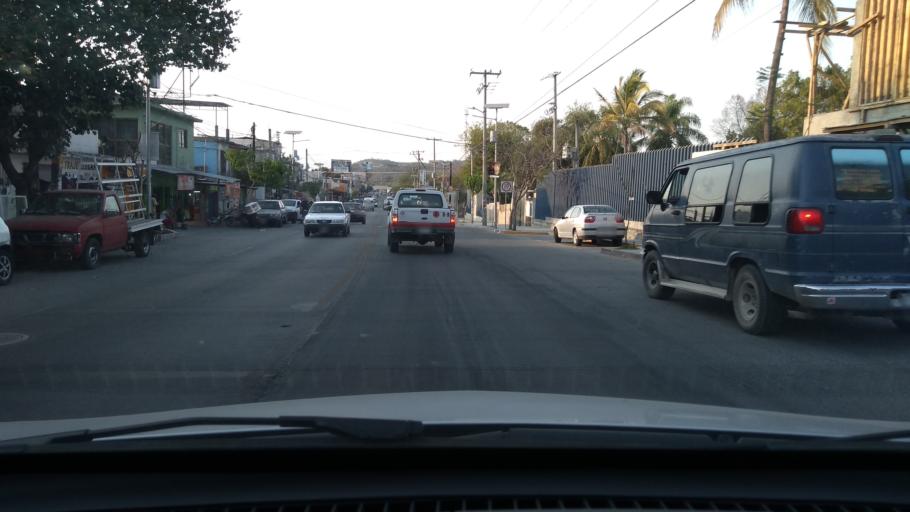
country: MX
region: Morelos
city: Puente de Ixtla
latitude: 18.6251
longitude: -99.3217
